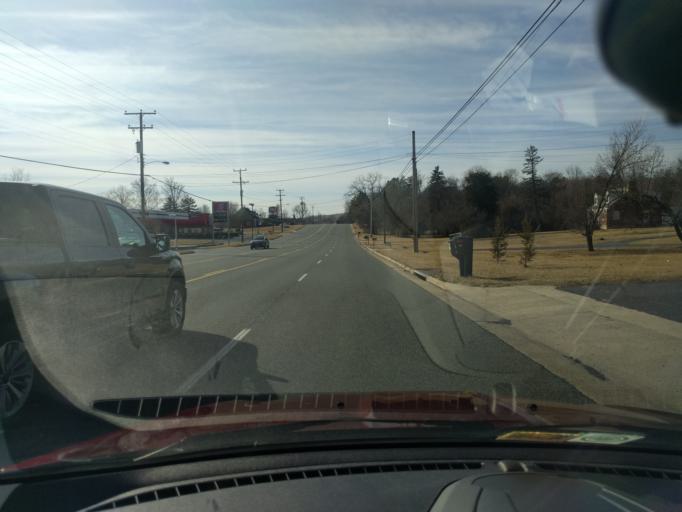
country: US
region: Virginia
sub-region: Augusta County
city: Verona
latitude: 38.1939
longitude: -79.0185
